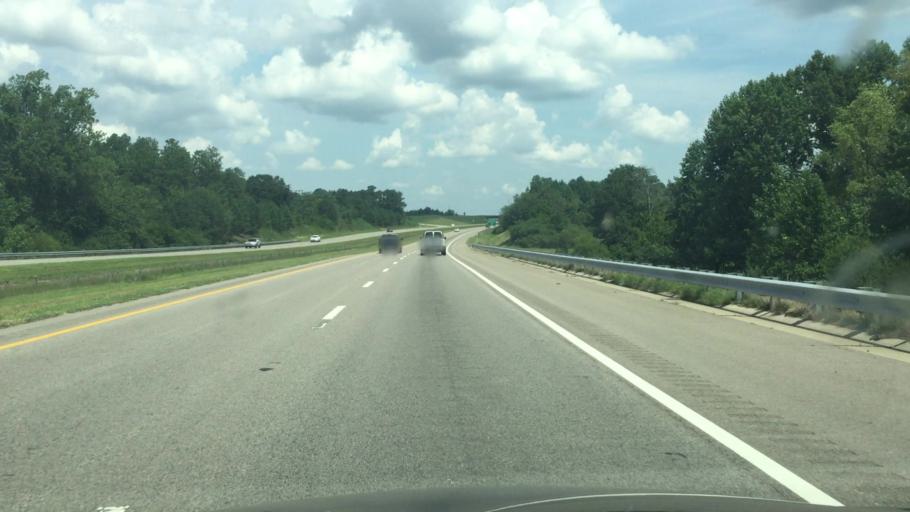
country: US
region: North Carolina
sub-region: Richmond County
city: Ellerbe
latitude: 35.1649
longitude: -79.7159
